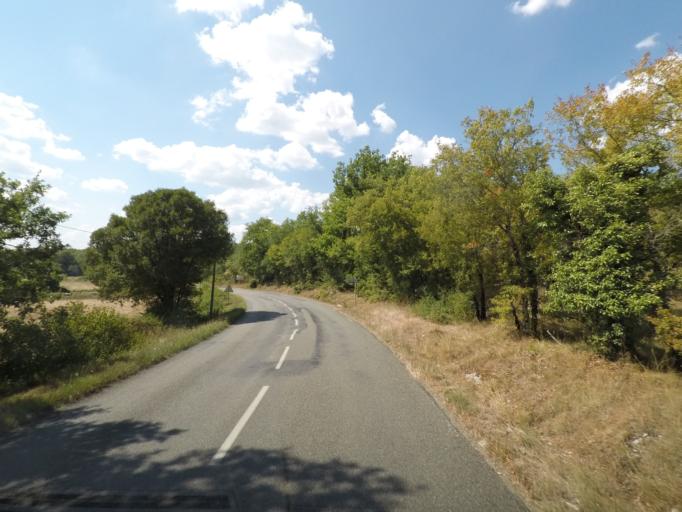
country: FR
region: Midi-Pyrenees
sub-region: Departement du Lot
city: Cahors
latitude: 44.5533
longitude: 1.5873
